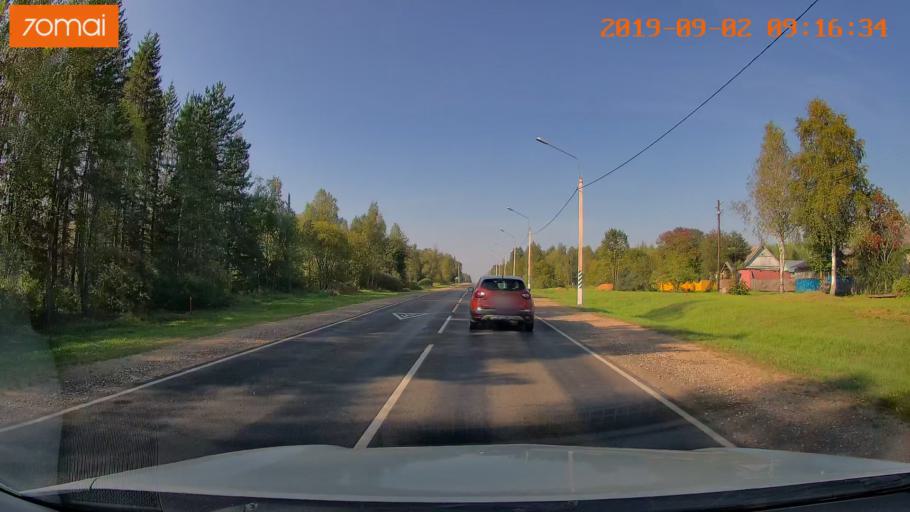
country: RU
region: Kaluga
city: Nikola-Lenivets
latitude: 54.8312
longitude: 35.4717
